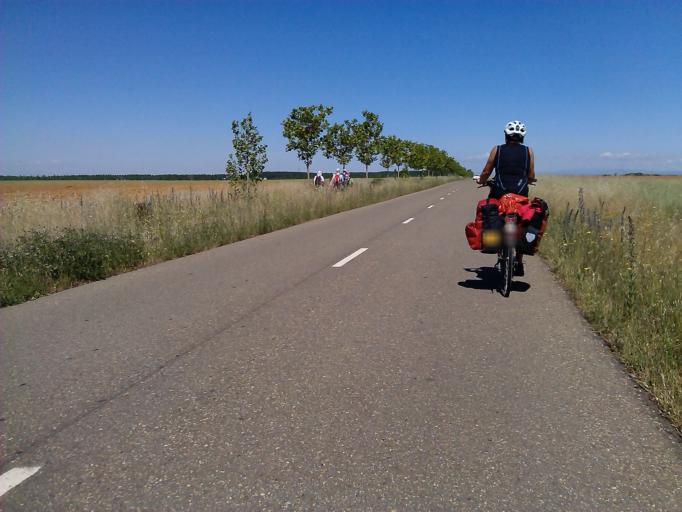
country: ES
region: Castille and Leon
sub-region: Provincia de Leon
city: Villamoratiel de las Matas
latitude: 42.4503
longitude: -5.2736
